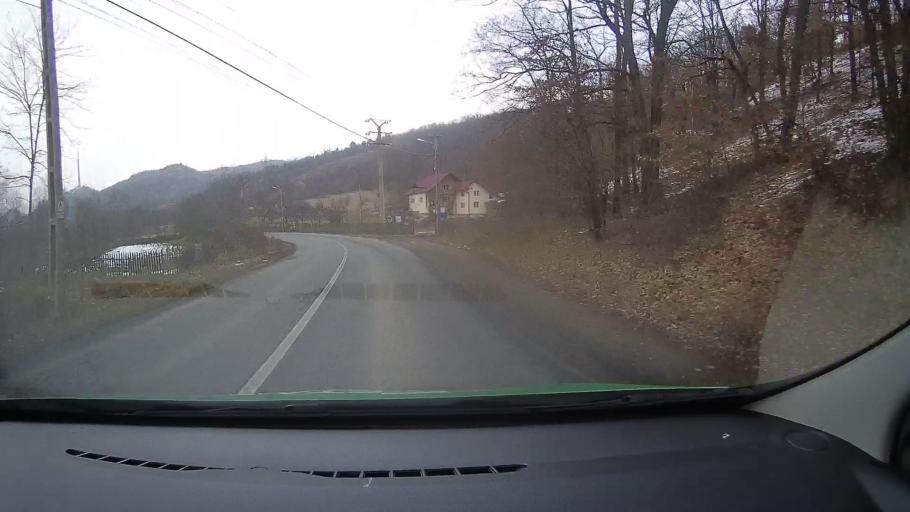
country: RO
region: Alba
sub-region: Oras Zlatna
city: Zlatna
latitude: 46.0944
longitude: 23.2555
